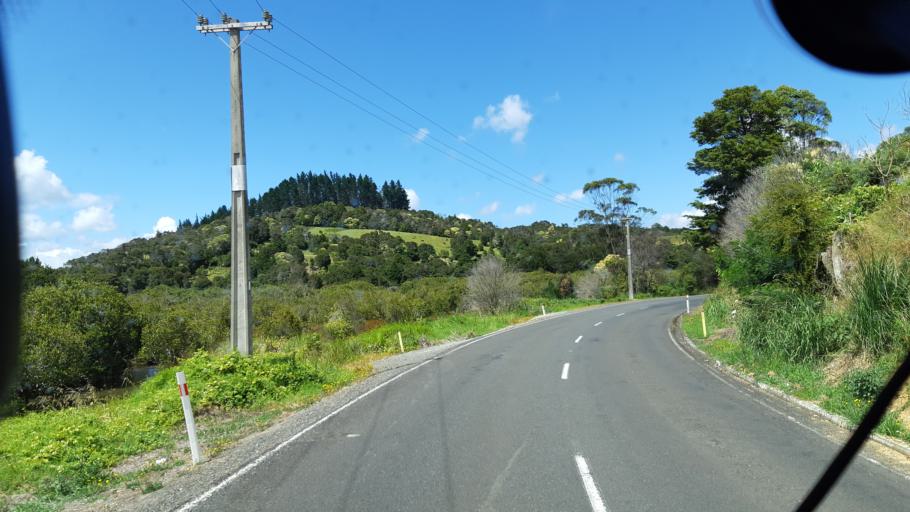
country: NZ
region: Northland
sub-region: Far North District
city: Taipa
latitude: -35.2745
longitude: 173.5212
